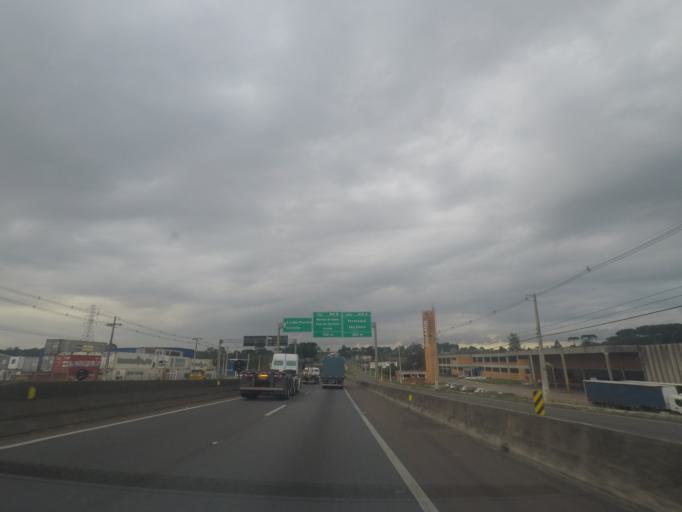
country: BR
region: Parana
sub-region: Sao Jose Dos Pinhais
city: Sao Jose dos Pinhais
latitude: -25.5772
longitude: -49.1789
